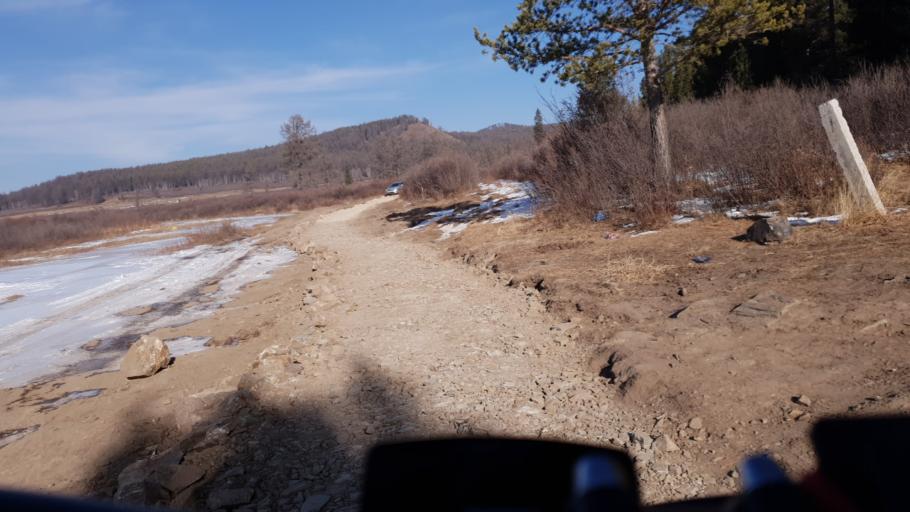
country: MN
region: Ulaanbaatar
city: Ulaanbaatar
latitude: 48.1600
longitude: 106.8828
